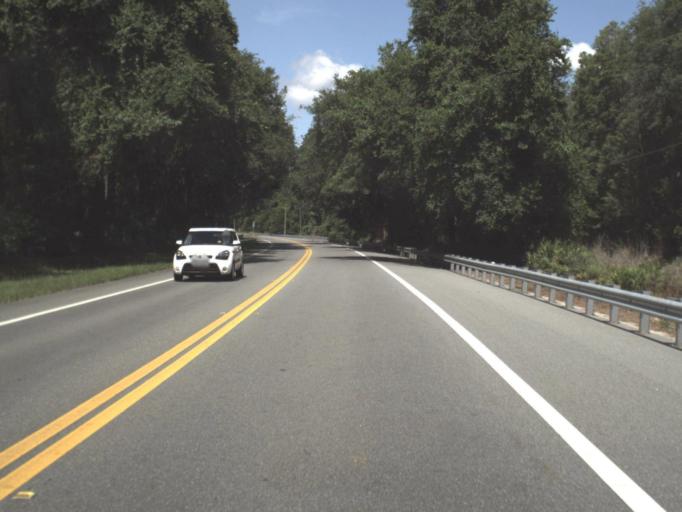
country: US
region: Florida
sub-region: Putnam County
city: Interlachen
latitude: 29.7316
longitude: -81.9088
